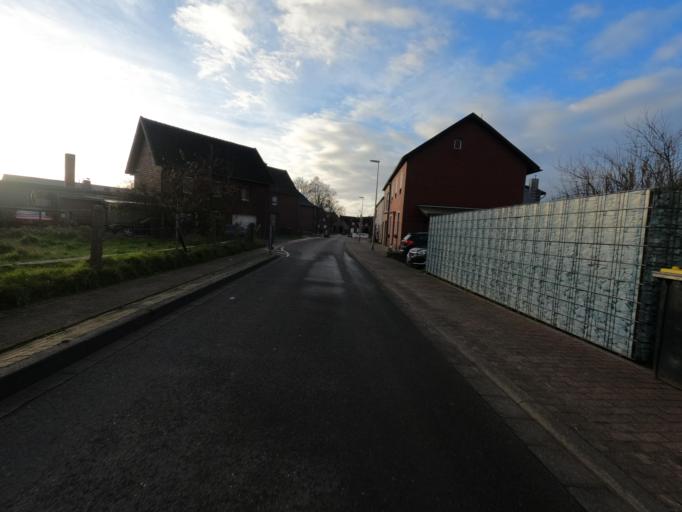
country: NL
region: Limburg
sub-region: Gemeente Roerdalen
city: Vlodrop
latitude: 51.0995
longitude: 6.0794
